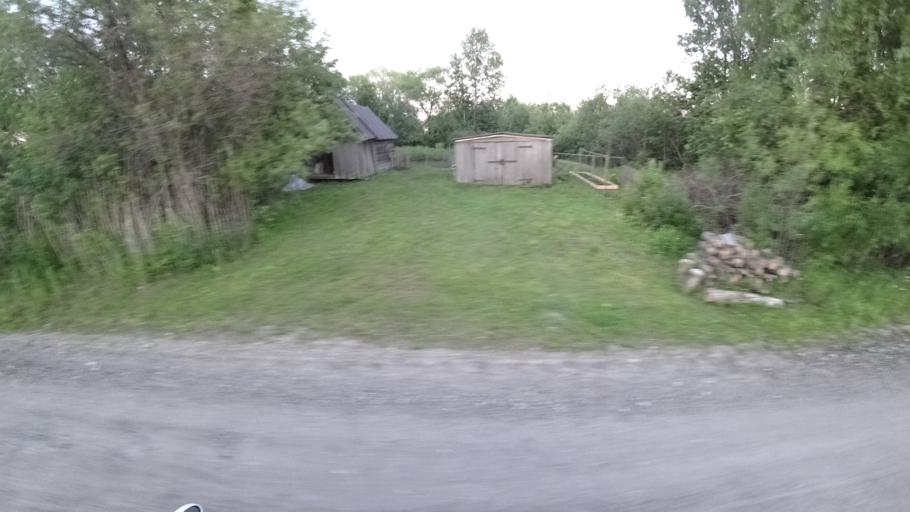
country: RU
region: Khabarovsk Krai
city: Khor
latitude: 47.8518
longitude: 134.9588
